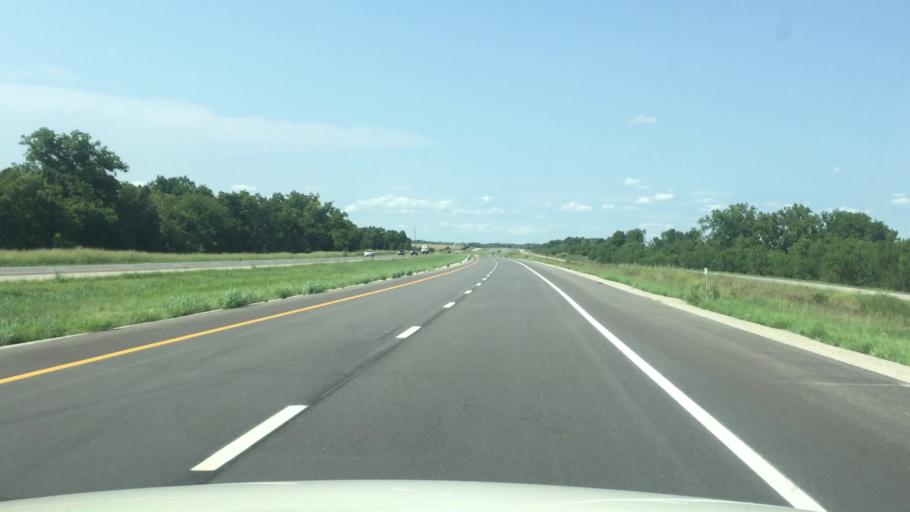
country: US
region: Kansas
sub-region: Linn County
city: La Cygne
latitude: 38.3051
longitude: -94.6773
